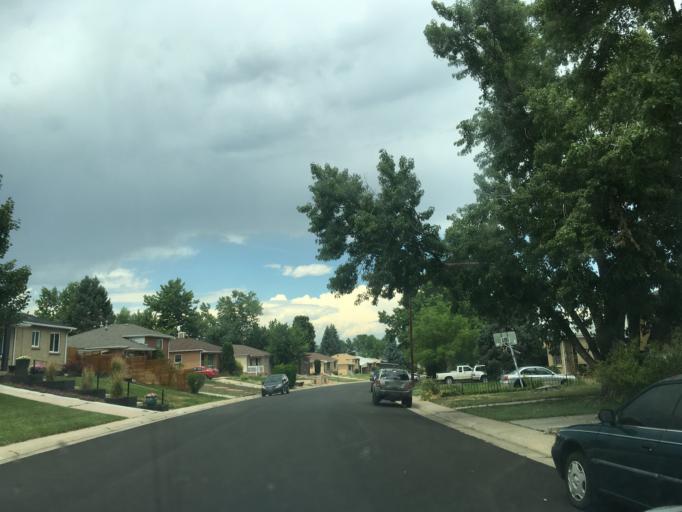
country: US
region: Colorado
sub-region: Arapahoe County
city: Sheridan
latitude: 39.6767
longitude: -105.0508
